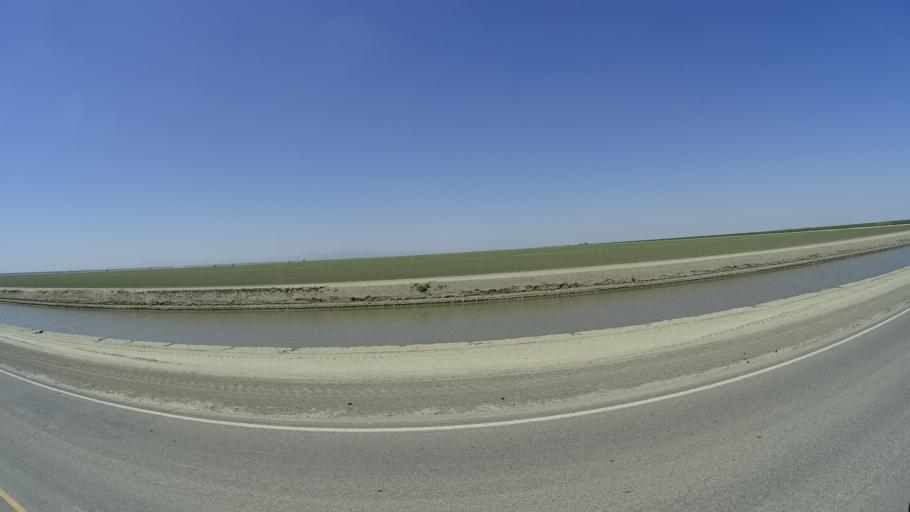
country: US
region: California
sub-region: Kings County
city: Corcoran
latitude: 36.0693
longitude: -119.6443
